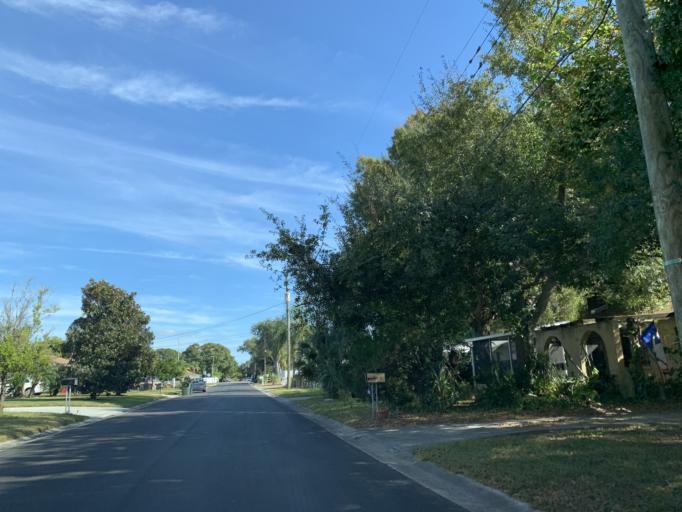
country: US
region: Florida
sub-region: Hillsborough County
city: Tampa
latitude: 27.8868
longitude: -82.5081
